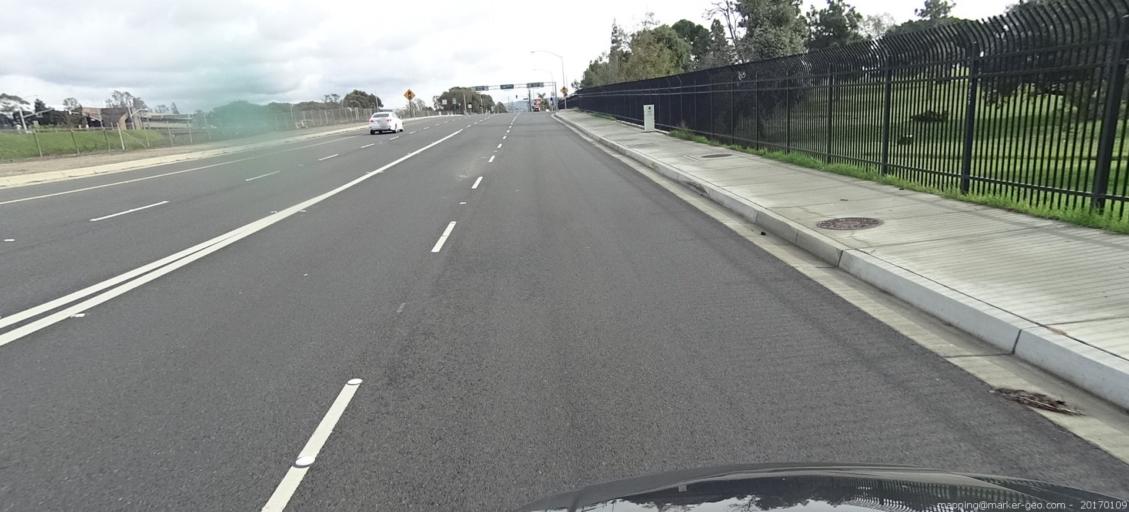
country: US
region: California
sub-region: Orange County
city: Costa Mesa
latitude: 33.6634
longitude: -117.8776
